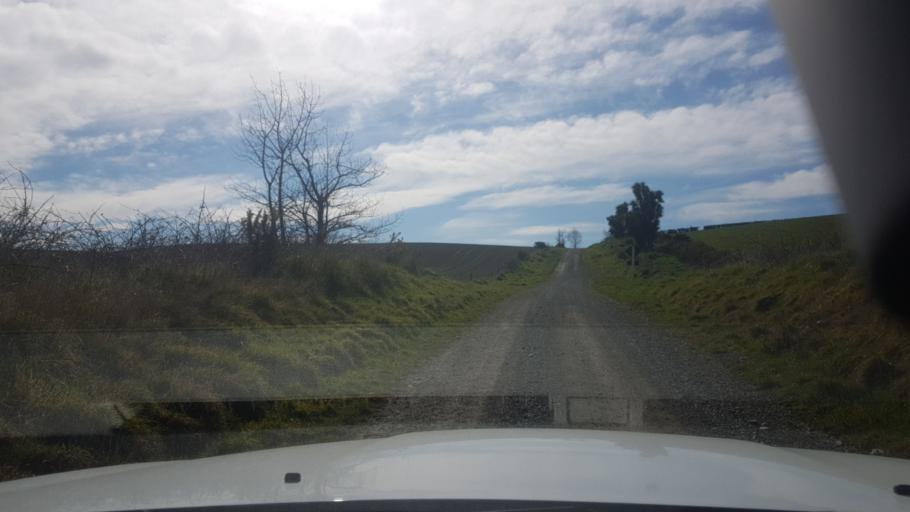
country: NZ
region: Canterbury
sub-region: Timaru District
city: Pleasant Point
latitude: -44.2013
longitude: 171.1870
